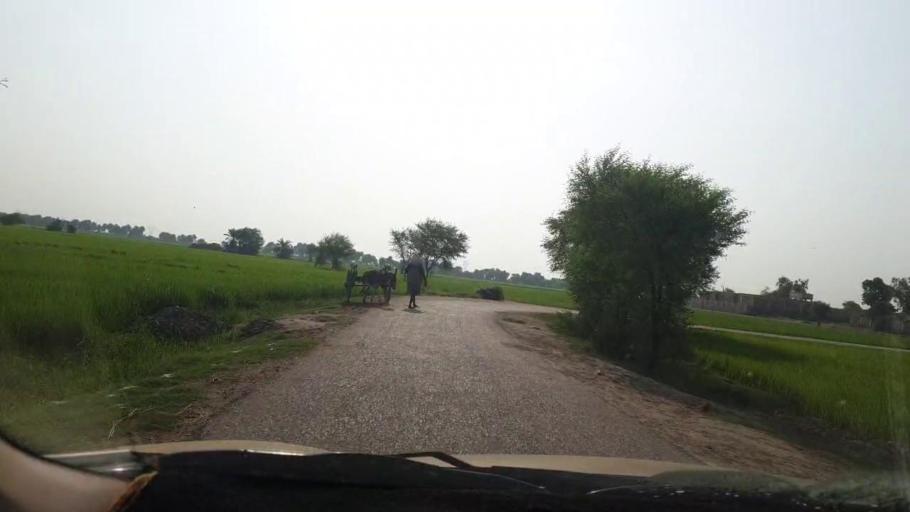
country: PK
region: Sindh
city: Goth Garelo
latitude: 27.4644
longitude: 68.0905
